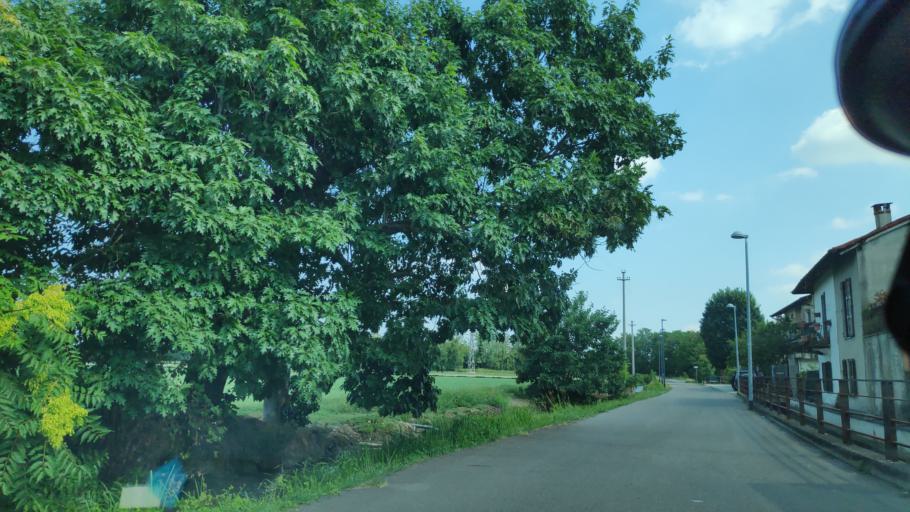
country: IT
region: Lombardy
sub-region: Citta metropolitana di Milano
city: Pieve Emanuele
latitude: 45.3618
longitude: 9.2067
